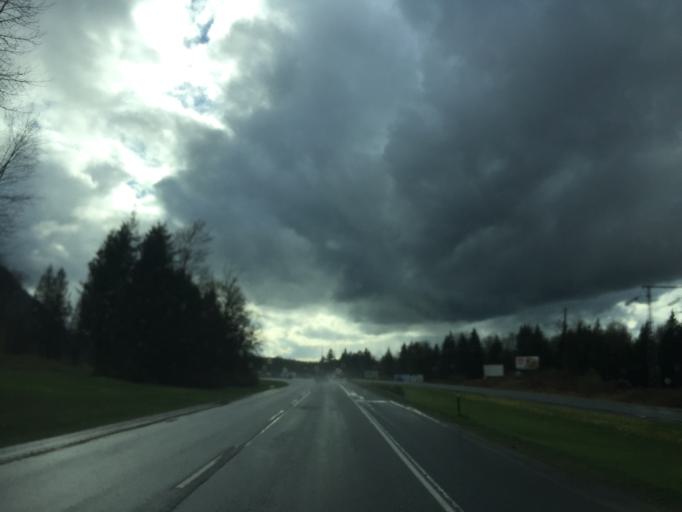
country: CA
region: British Columbia
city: Agassiz
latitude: 49.2054
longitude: -121.7161
